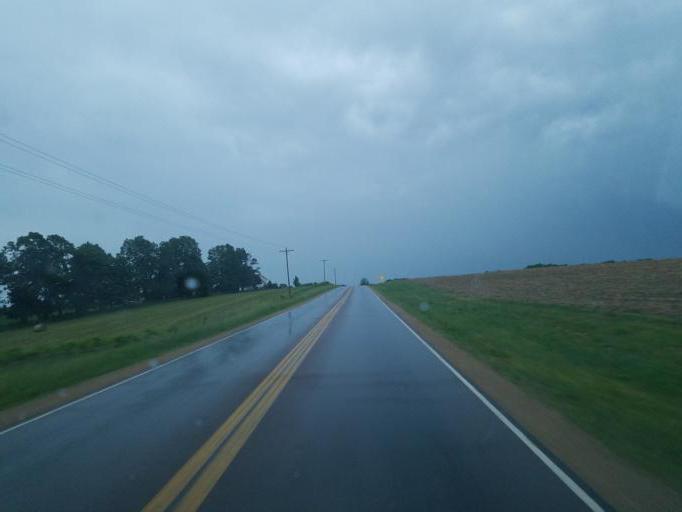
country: US
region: Wisconsin
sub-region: Vernon County
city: Hillsboro
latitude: 43.6502
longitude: -90.4537
